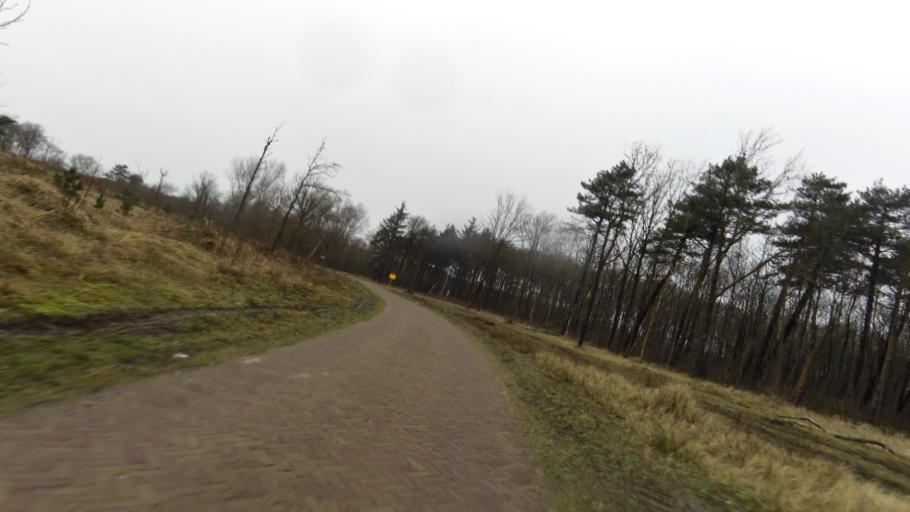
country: NL
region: North Holland
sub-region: Gemeente Bergen
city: Egmond aan Zee
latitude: 52.5751
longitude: 4.6255
